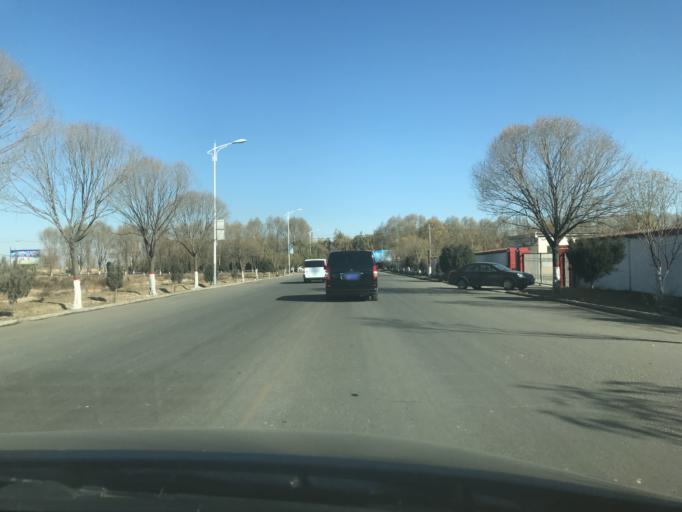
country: CN
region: Gansu Sheng
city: Gulang
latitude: 37.6796
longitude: 102.8363
